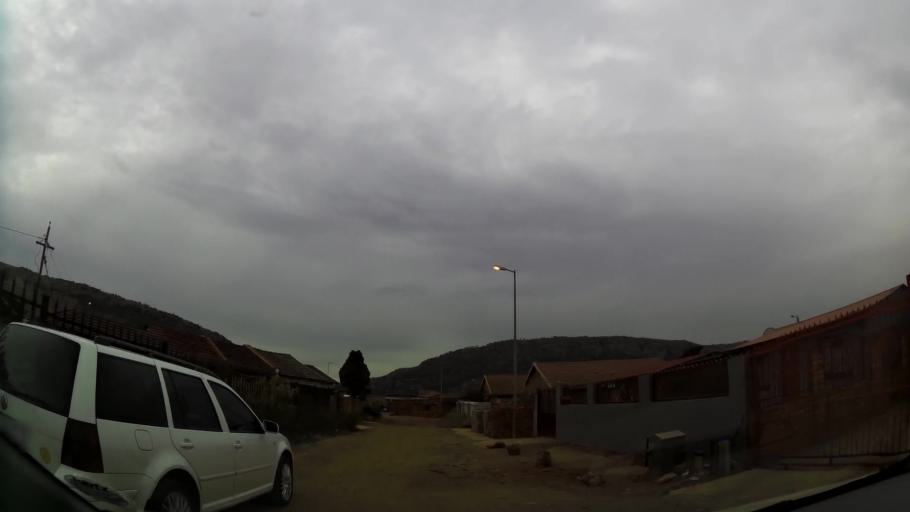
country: ZA
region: Gauteng
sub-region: City of Tshwane Metropolitan Municipality
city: Cullinan
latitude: -25.7067
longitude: 28.3570
